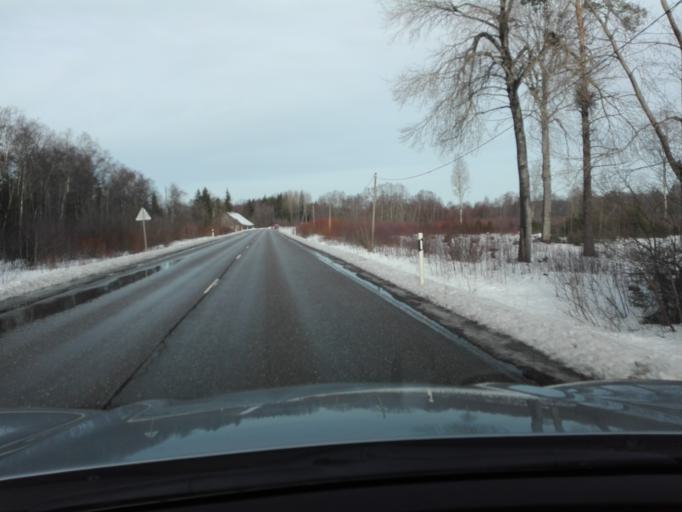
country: EE
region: Raplamaa
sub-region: Rapla vald
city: Rapla
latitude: 58.9661
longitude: 24.7667
